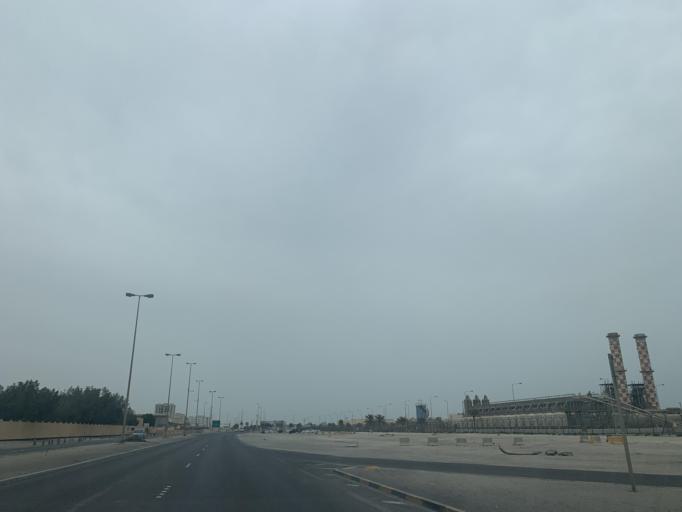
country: BH
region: Muharraq
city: Al Hadd
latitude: 26.2193
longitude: 50.6577
